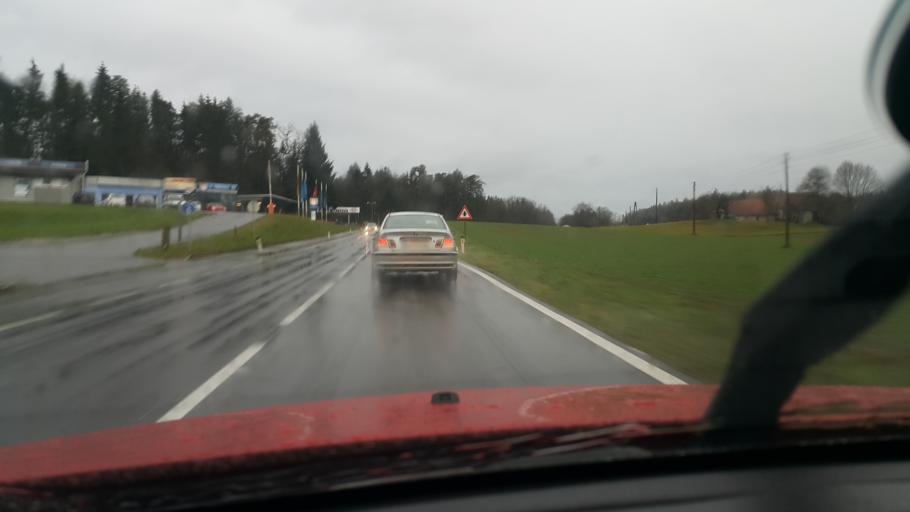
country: AT
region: Styria
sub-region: Politischer Bezirk Leibnitz
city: Hengsberg
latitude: 46.8609
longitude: 15.4442
